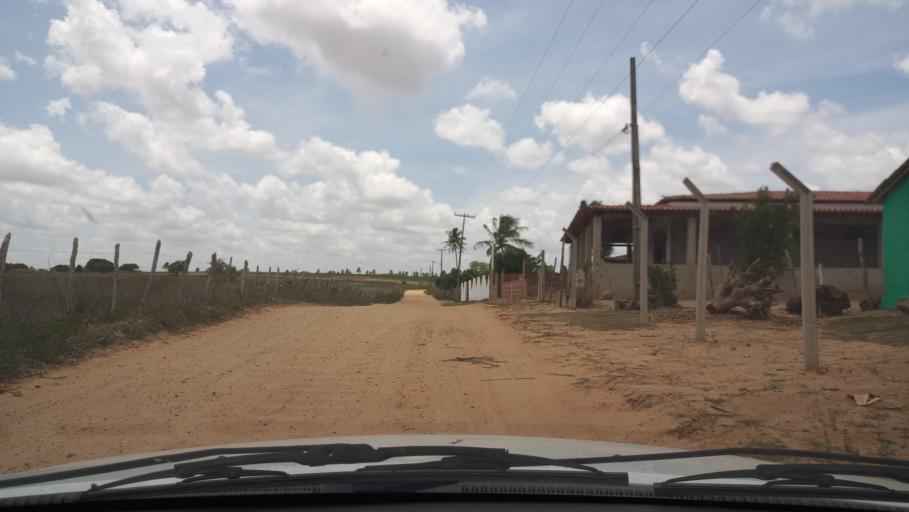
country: BR
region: Rio Grande do Norte
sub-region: Brejinho
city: Brejinho
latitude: -6.3022
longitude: -35.3456
